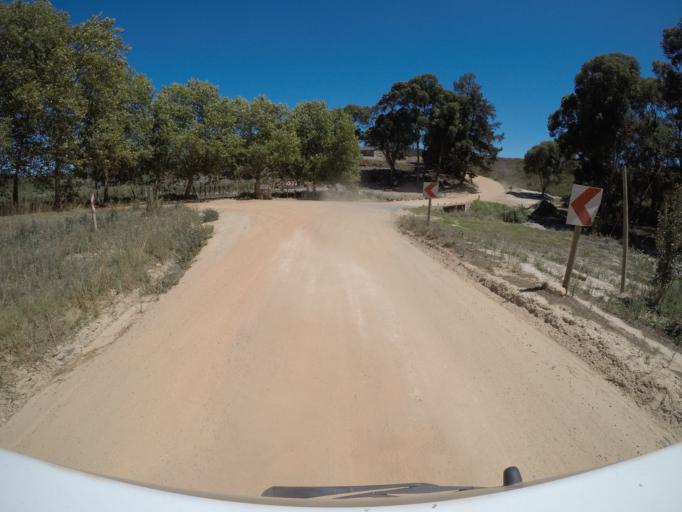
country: ZA
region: Western Cape
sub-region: Overberg District Municipality
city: Grabouw
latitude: -34.2438
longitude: 19.0958
